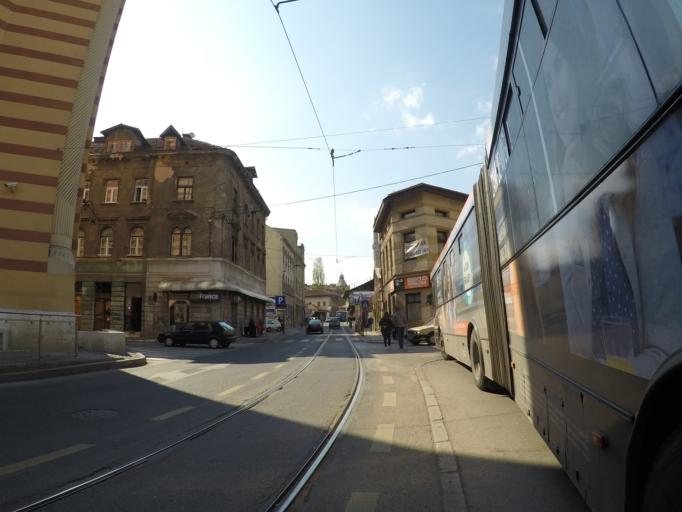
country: BA
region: Federation of Bosnia and Herzegovina
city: Kobilja Glava
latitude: 43.8595
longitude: 18.4333
